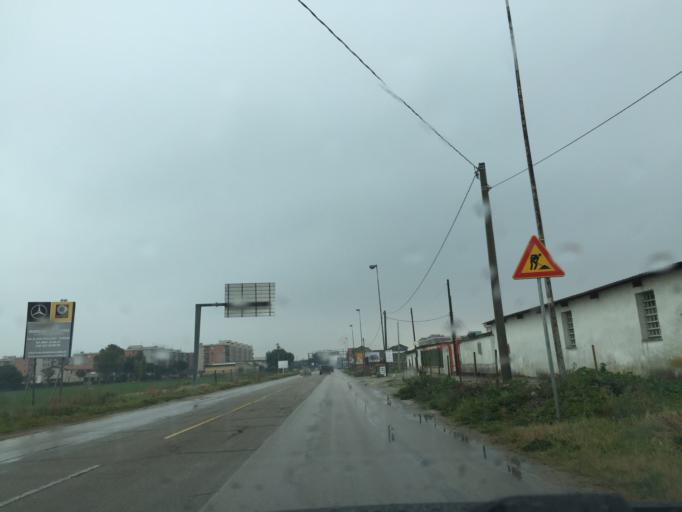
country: IT
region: Apulia
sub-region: Provincia di Foggia
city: Foggia
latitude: 41.4696
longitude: 15.5168
